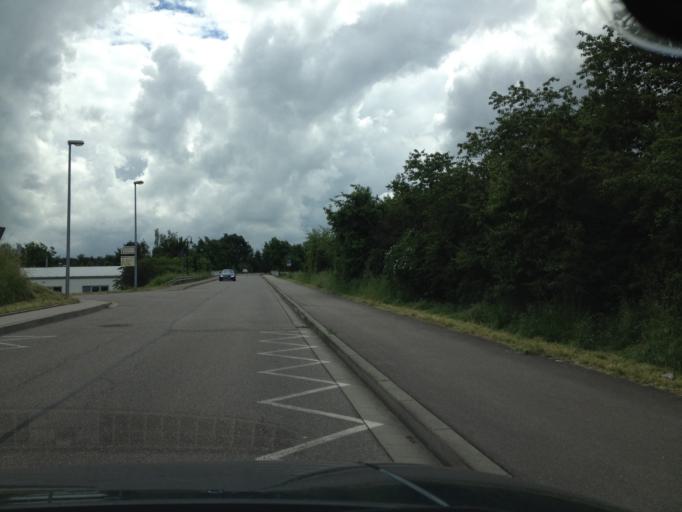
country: DE
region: Saarland
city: Bexbach
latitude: 49.3093
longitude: 7.2700
